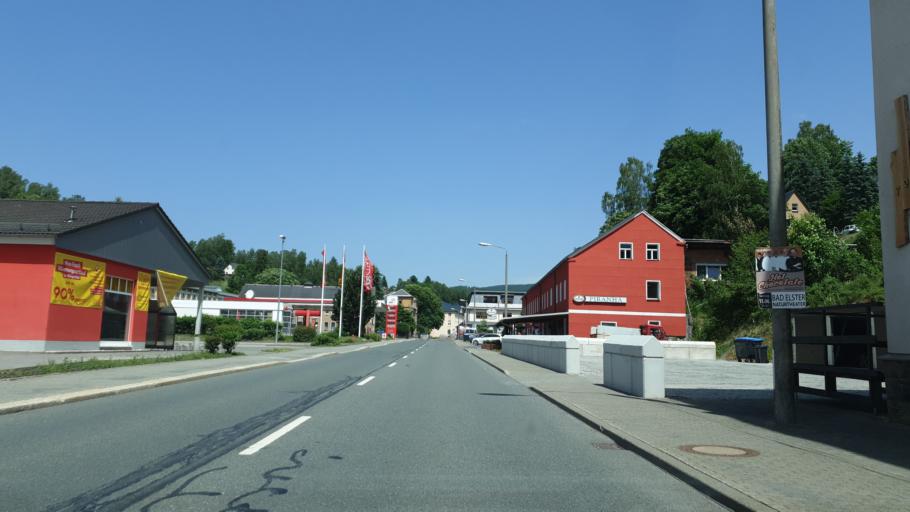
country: DE
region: Saxony
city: Klingenthal
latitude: 50.3644
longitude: 12.4689
